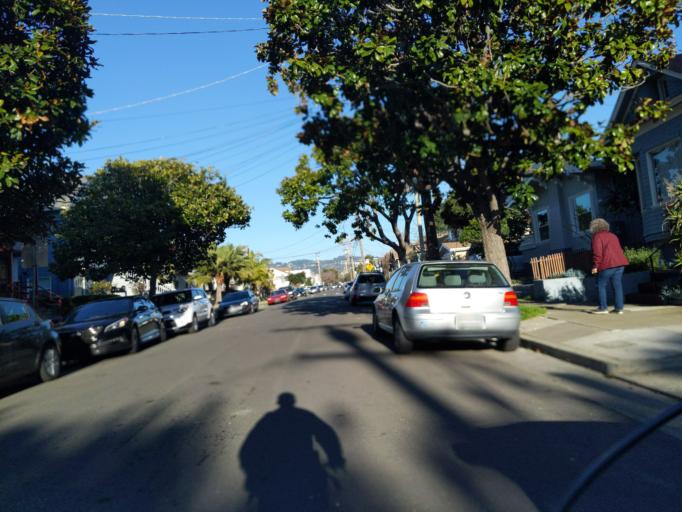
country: US
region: California
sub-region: Alameda County
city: Emeryville
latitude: 37.8395
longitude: -122.2787
